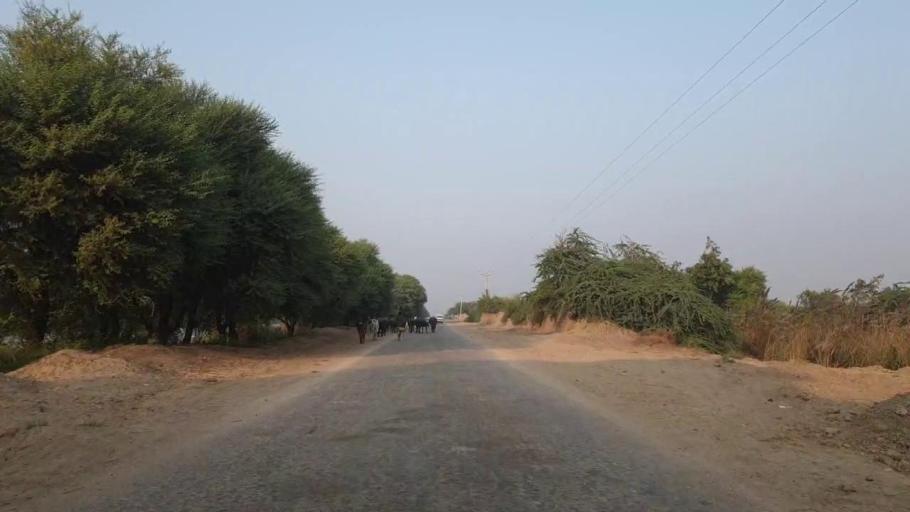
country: PK
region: Sindh
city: Tando Muhammad Khan
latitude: 25.1263
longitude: 68.4316
